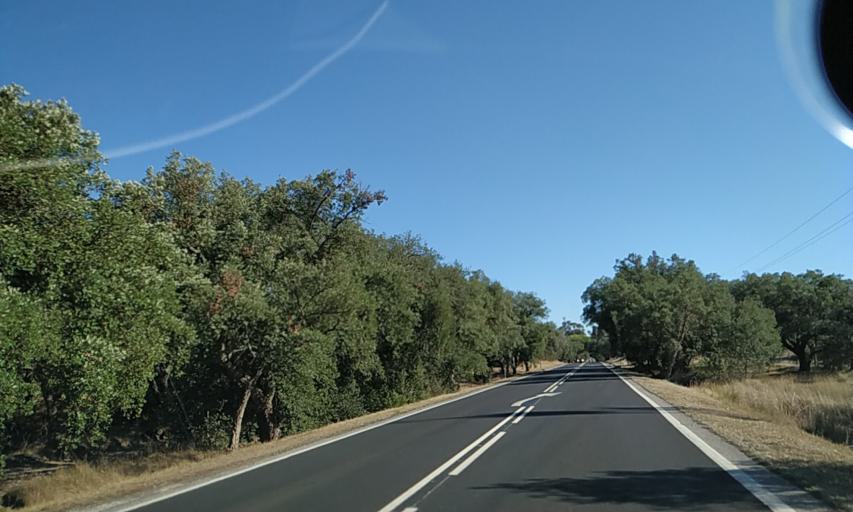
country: PT
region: Santarem
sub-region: Benavente
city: Poceirao
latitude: 38.8412
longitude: -8.8810
